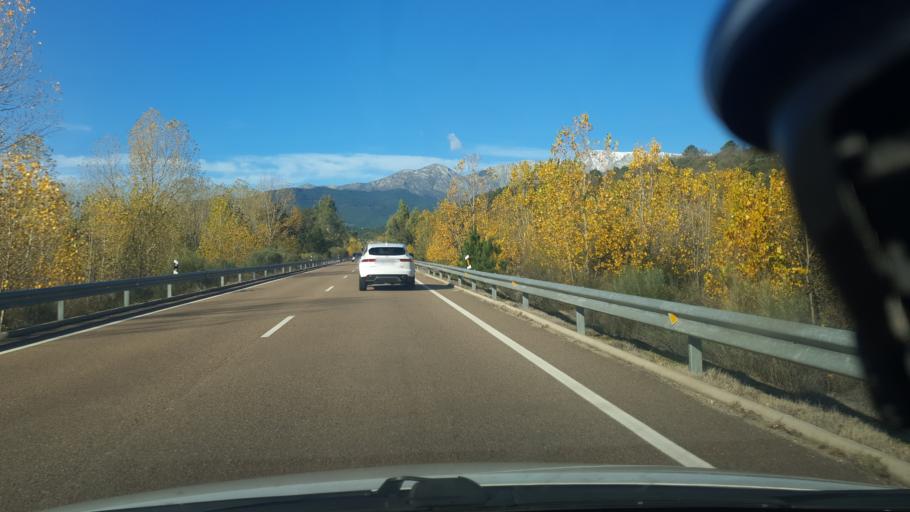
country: ES
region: Castille and Leon
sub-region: Provincia de Avila
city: Arenas de San Pedro
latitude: 40.1874
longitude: -5.0616
